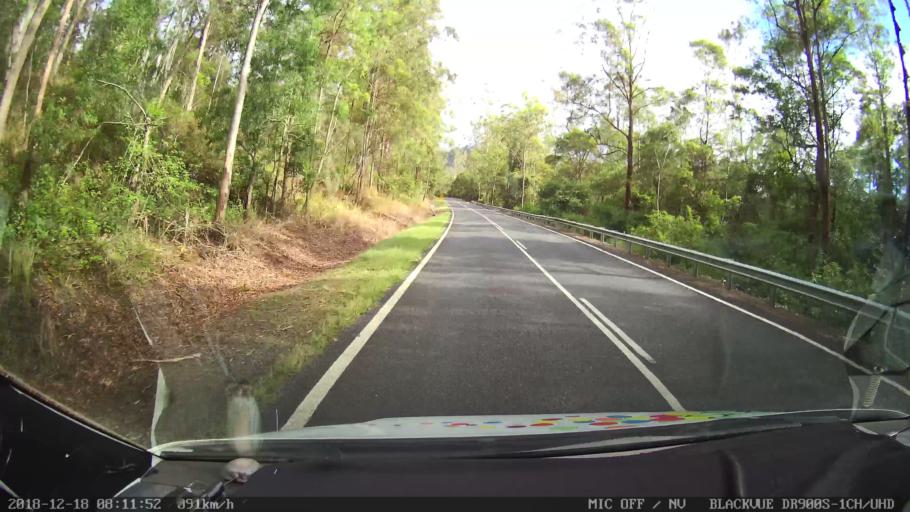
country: AU
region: New South Wales
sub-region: Kyogle
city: Kyogle
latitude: -28.3454
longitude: 152.6703
